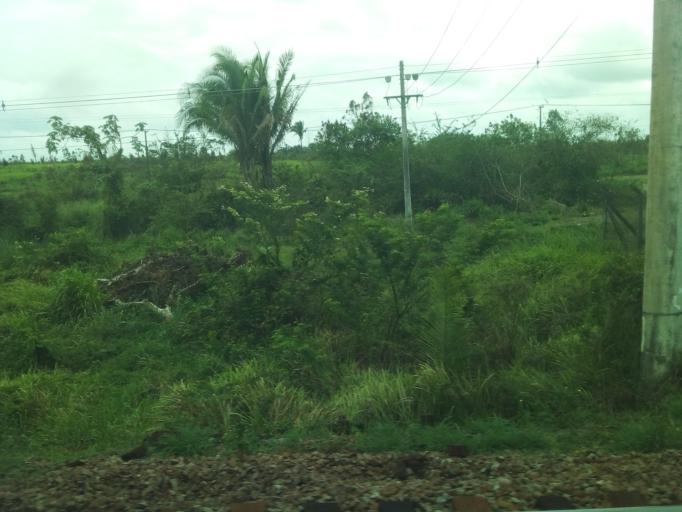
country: BR
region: Maranhao
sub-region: Santa Ines
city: Santa Ines
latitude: -3.6979
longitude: -45.4102
